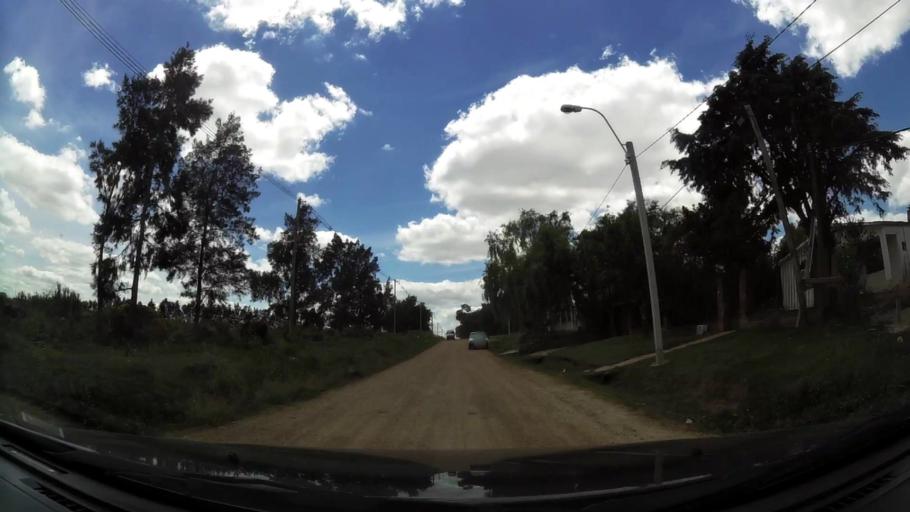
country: UY
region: Canelones
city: Colonia Nicolich
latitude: -34.8187
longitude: -56.0031
